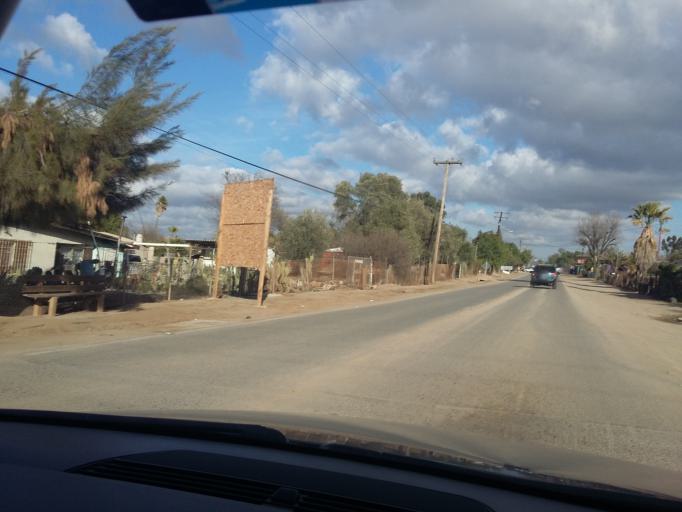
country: MX
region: Baja California
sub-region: Ensenada
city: Rancho Verde
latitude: 32.0742
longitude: -116.6283
